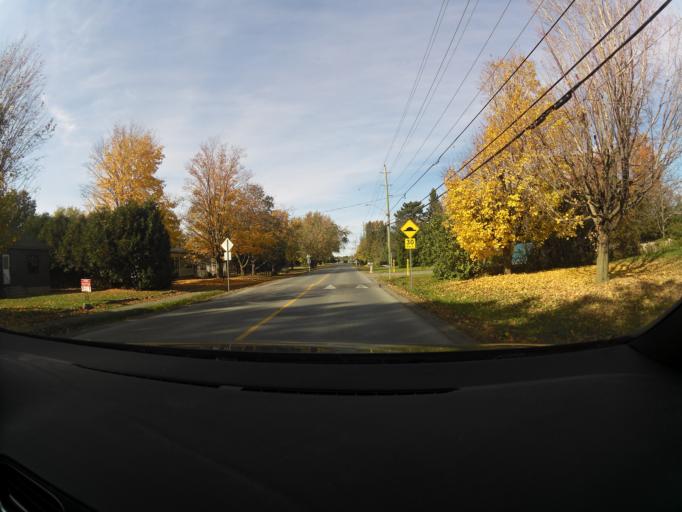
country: CA
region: Ontario
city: Bells Corners
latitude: 45.2783
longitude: -75.9230
